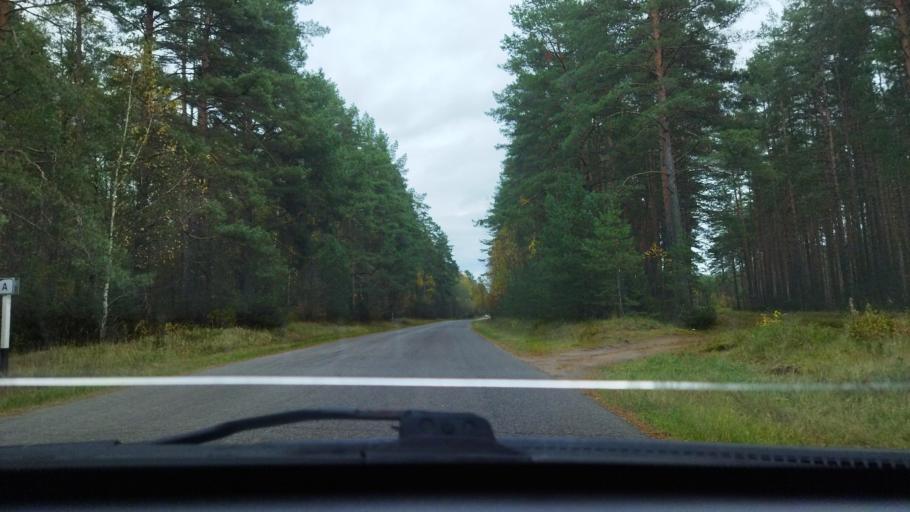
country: BY
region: Minsk
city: Svir
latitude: 54.8037
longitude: 26.2427
